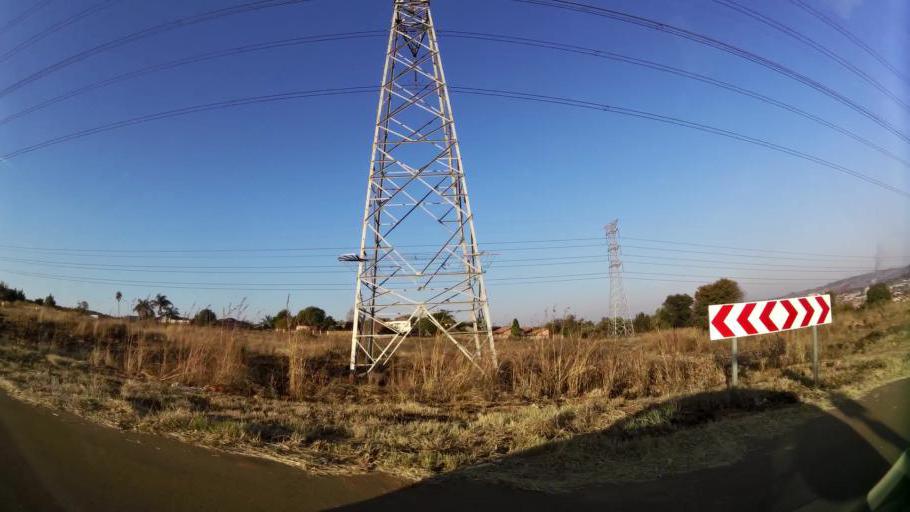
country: ZA
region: Gauteng
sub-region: City of Tshwane Metropolitan Municipality
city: Pretoria
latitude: -25.7426
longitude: 28.1055
